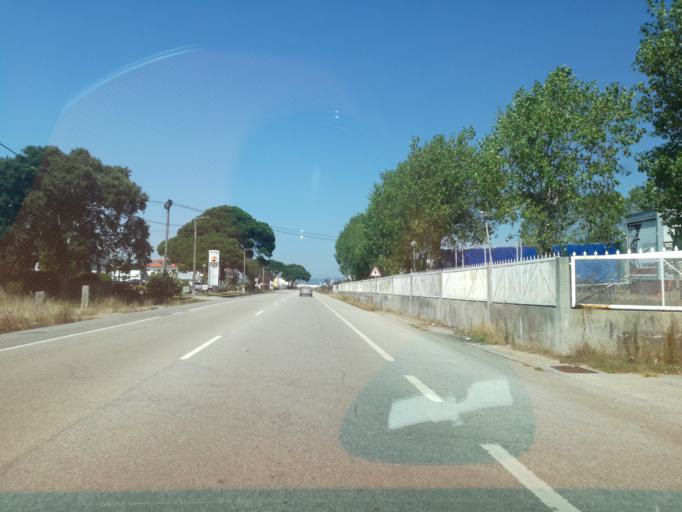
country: PT
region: Braga
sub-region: Esposende
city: Apulia
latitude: 41.4598
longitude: -8.7495
